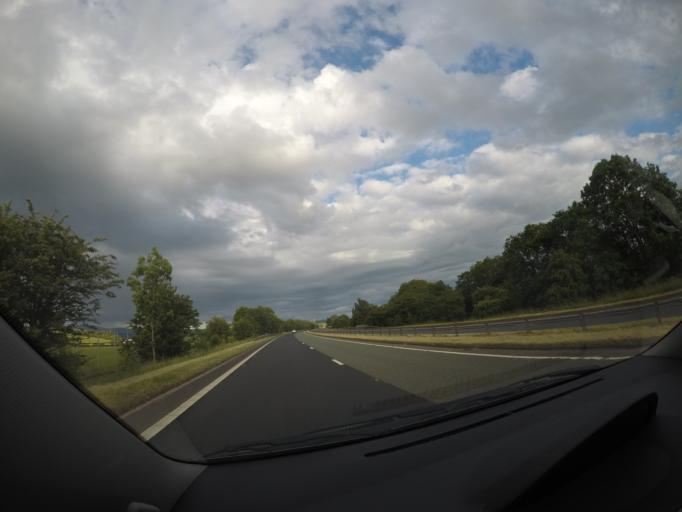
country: GB
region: England
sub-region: Cumbria
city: Penrith
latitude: 54.6571
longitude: -2.7221
